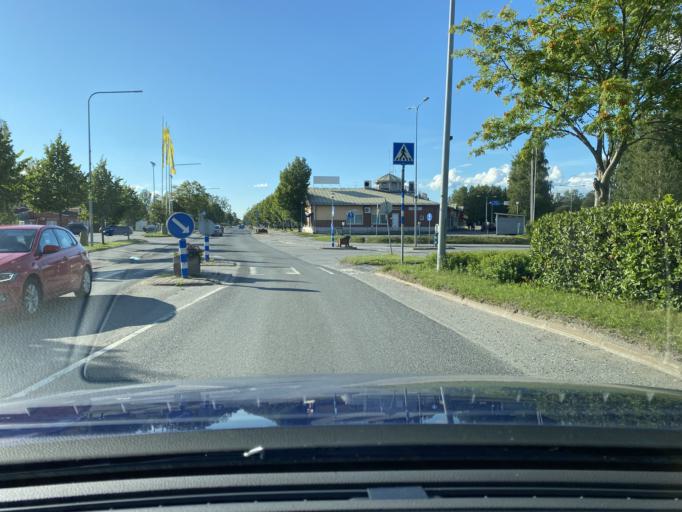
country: FI
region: Ostrobothnia
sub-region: Kyroenmaa
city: Laihia
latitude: 62.9784
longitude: 22.0107
